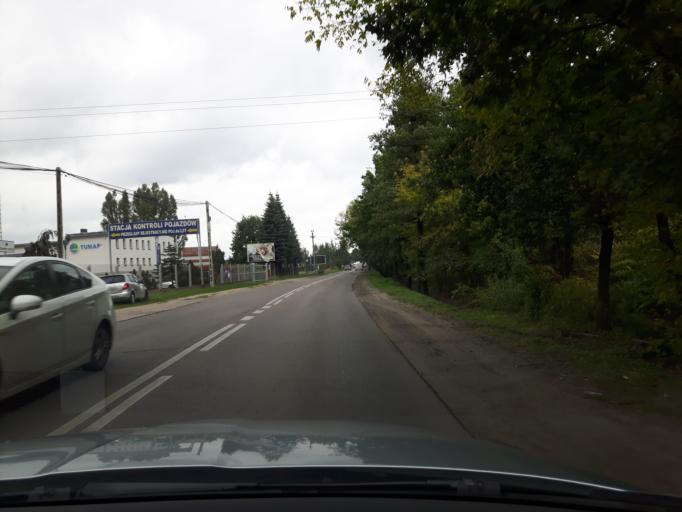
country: PL
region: Masovian Voivodeship
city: Zielonka
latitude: 52.3080
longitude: 21.1697
